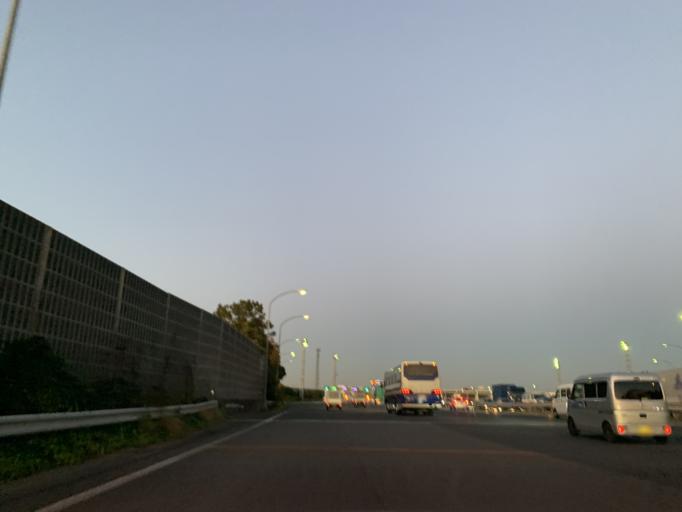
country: JP
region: Chiba
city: Nagareyama
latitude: 35.8632
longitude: 139.8814
